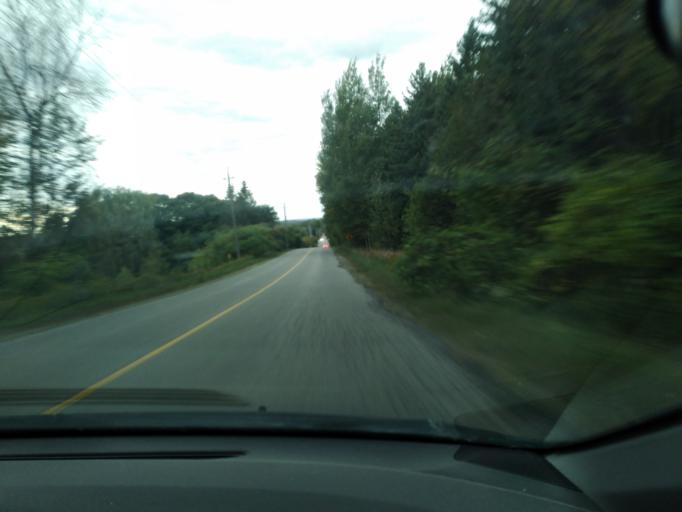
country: CA
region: Ontario
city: Bradford West Gwillimbury
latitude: 43.9501
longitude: -79.7794
